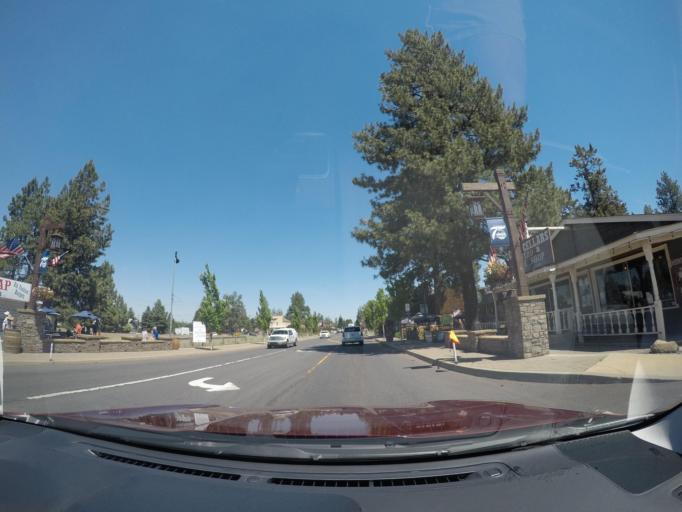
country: US
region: Oregon
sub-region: Deschutes County
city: Sisters
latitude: 44.2913
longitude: -121.5537
